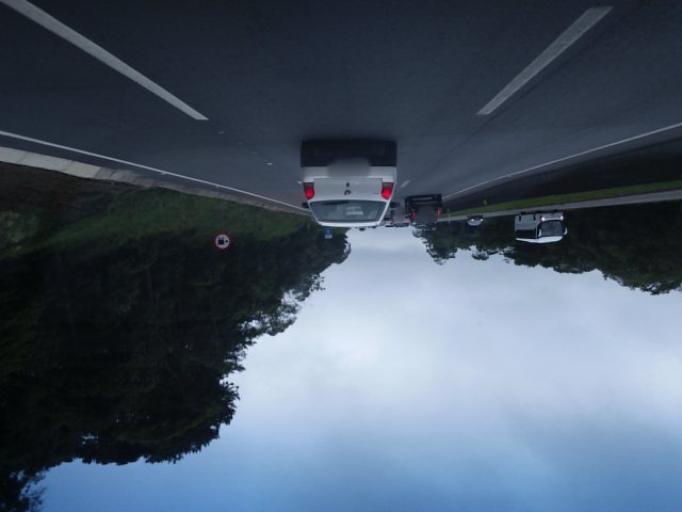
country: BR
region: Parana
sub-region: Sao Jose Dos Pinhais
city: Sao Jose dos Pinhais
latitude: -25.8195
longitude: -49.1288
